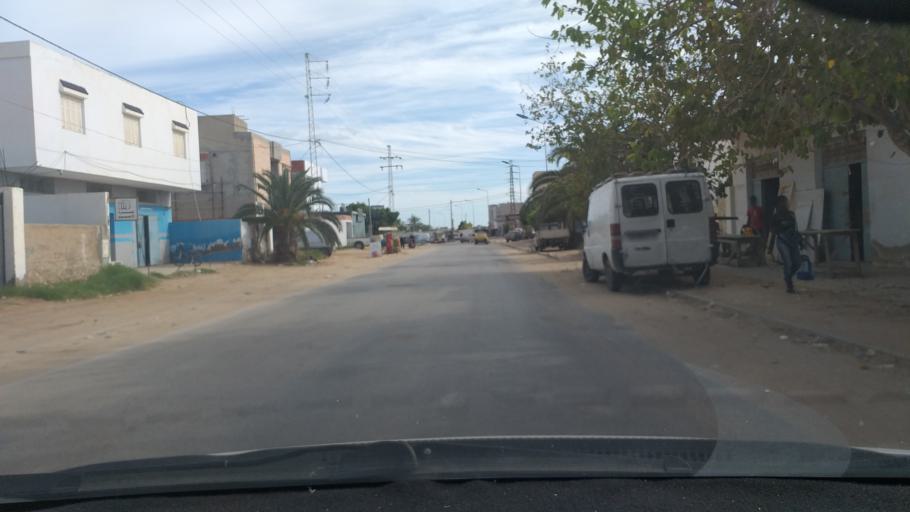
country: TN
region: Safaqis
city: Al Qarmadah
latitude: 34.7921
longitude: 10.8047
